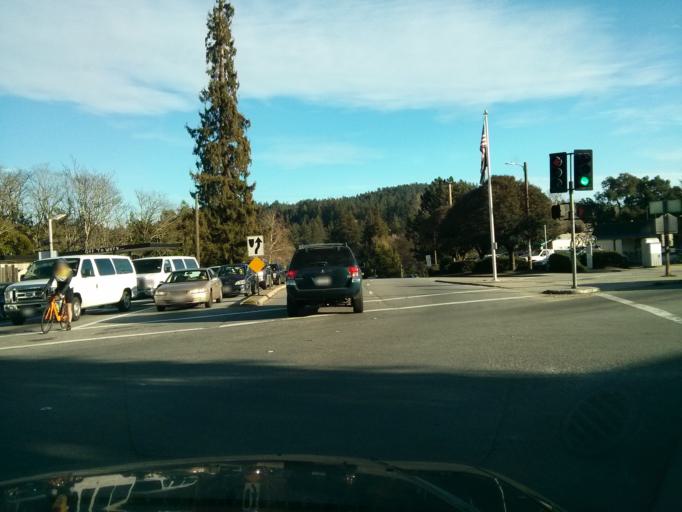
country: US
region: California
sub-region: Santa Cruz County
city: Felton
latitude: 37.0530
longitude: -122.0732
